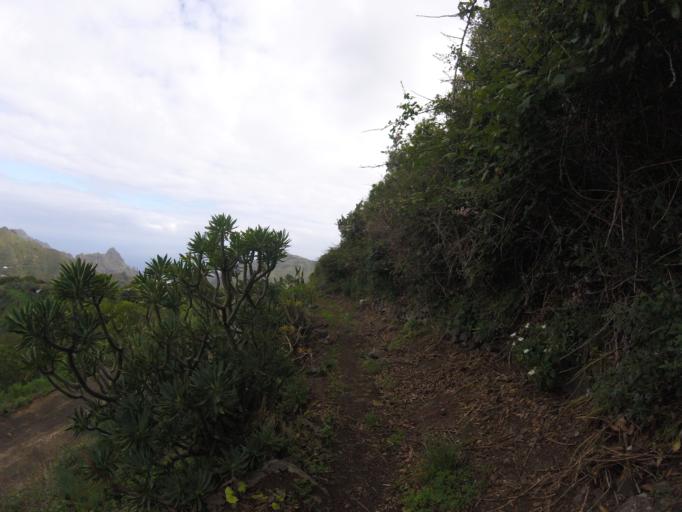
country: ES
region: Canary Islands
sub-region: Provincia de Santa Cruz de Tenerife
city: Tegueste
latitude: 28.5447
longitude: -16.2859
